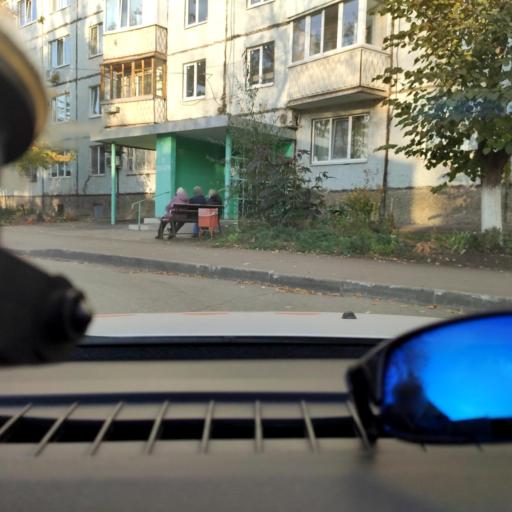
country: RU
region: Samara
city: Samara
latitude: 53.2615
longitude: 50.2212
